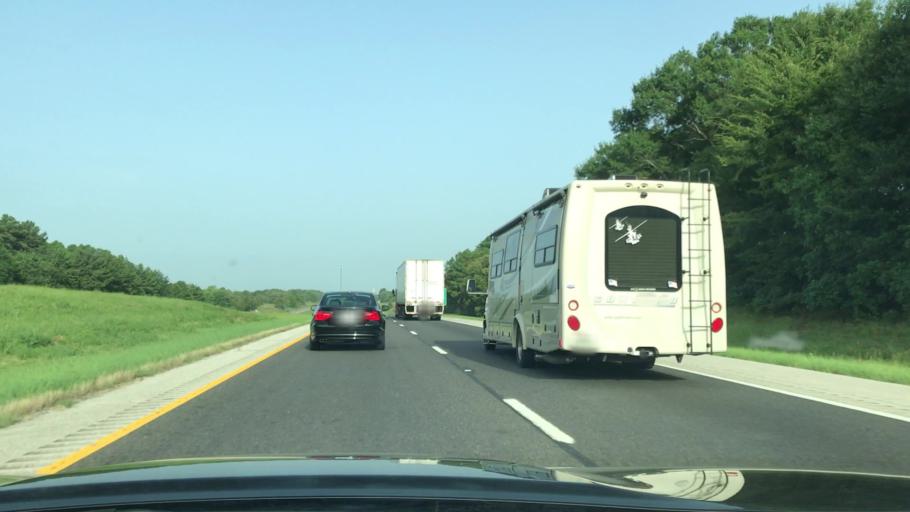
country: US
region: Texas
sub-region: Smith County
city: Tyler
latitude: 32.4527
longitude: -95.2597
